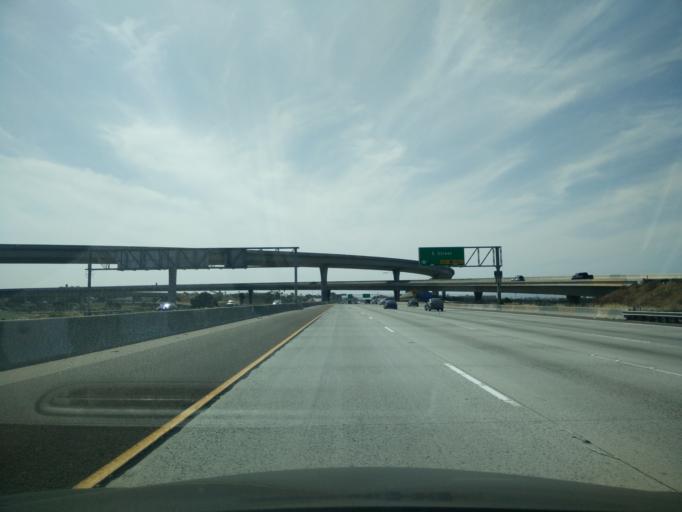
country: US
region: California
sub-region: San Diego County
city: Chula Vista
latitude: 32.6528
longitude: -117.1050
